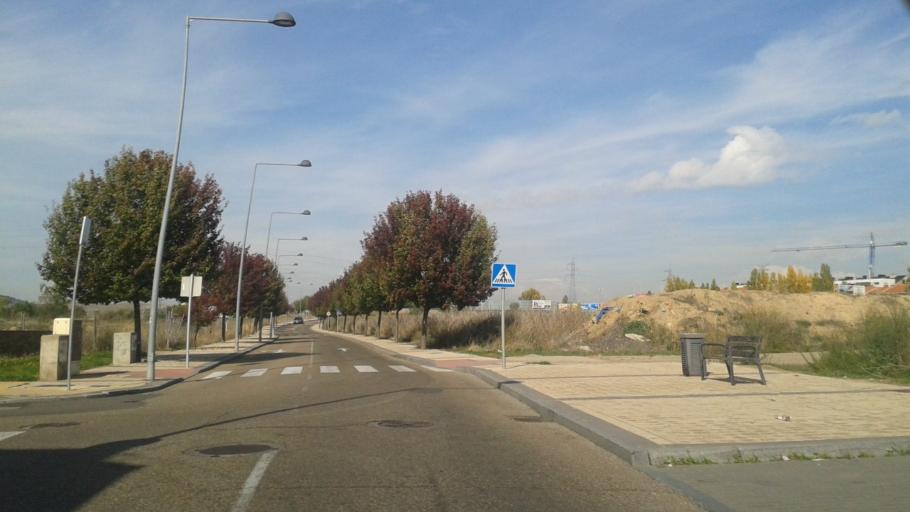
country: ES
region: Castille and Leon
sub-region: Provincia de Valladolid
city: Zaratan
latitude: 41.6311
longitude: -4.7726
